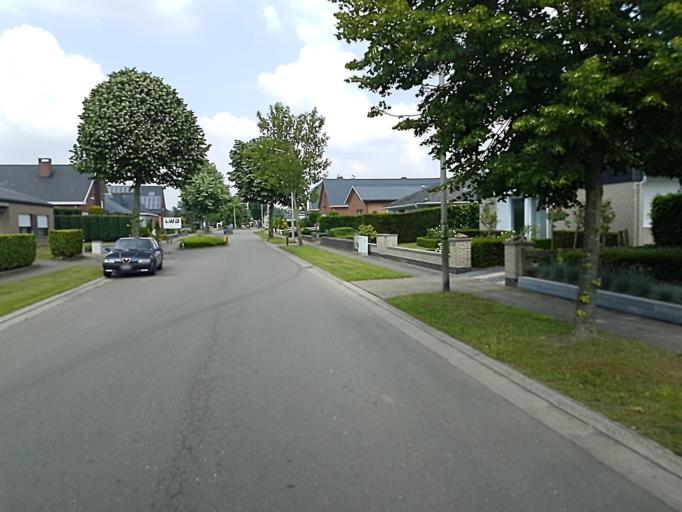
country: BE
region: Flanders
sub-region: Provincie Vlaams-Brabant
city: Londerzeel
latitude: 51.0120
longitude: 4.3072
